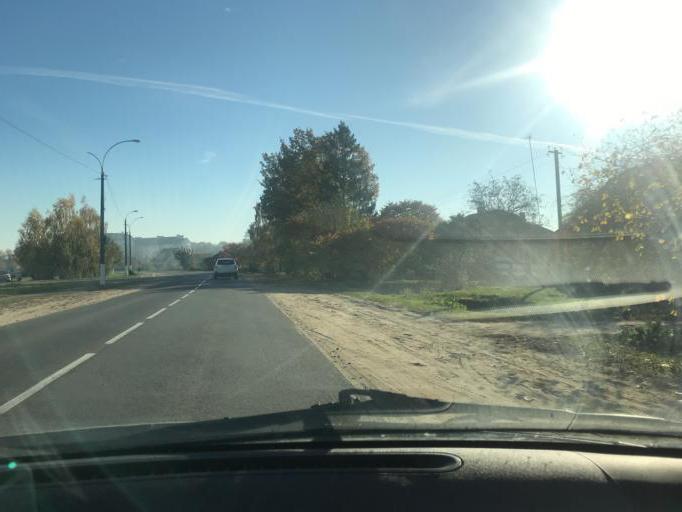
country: BY
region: Brest
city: Ivanava
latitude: 52.1431
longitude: 25.5212
